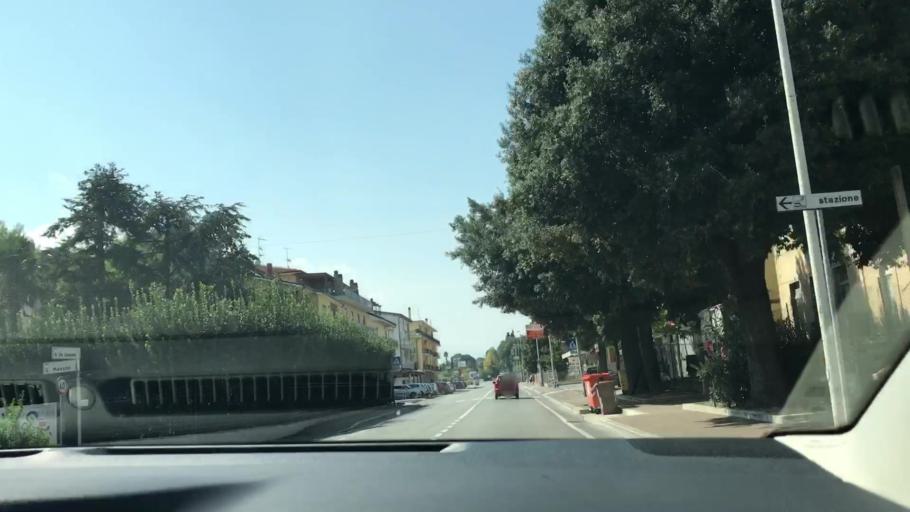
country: IT
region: The Marches
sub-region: Provincia di Ascoli Piceno
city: Centobuchi
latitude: 42.8974
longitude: 13.8485
